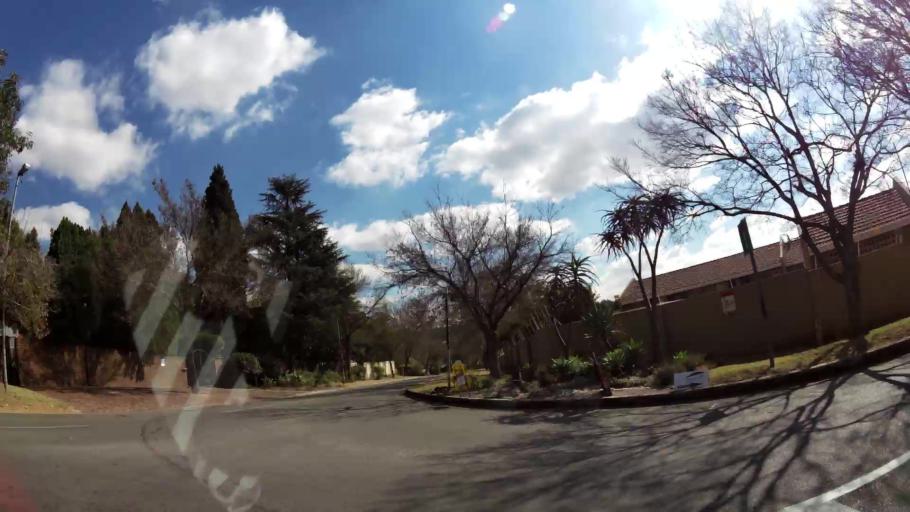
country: ZA
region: Gauteng
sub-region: City of Johannesburg Metropolitan Municipality
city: Roodepoort
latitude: -26.0721
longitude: 27.9685
